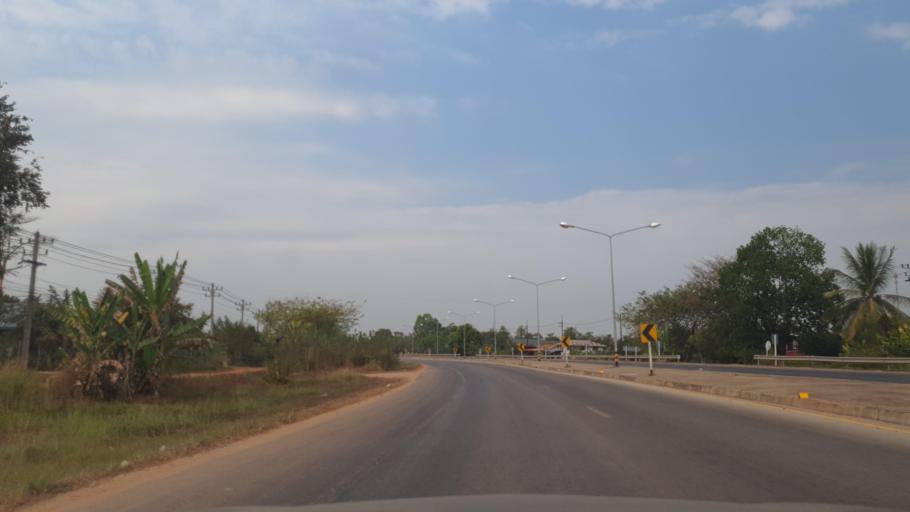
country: TH
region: Changwat Bueng Kan
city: Si Wilai
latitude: 18.3034
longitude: 103.8140
